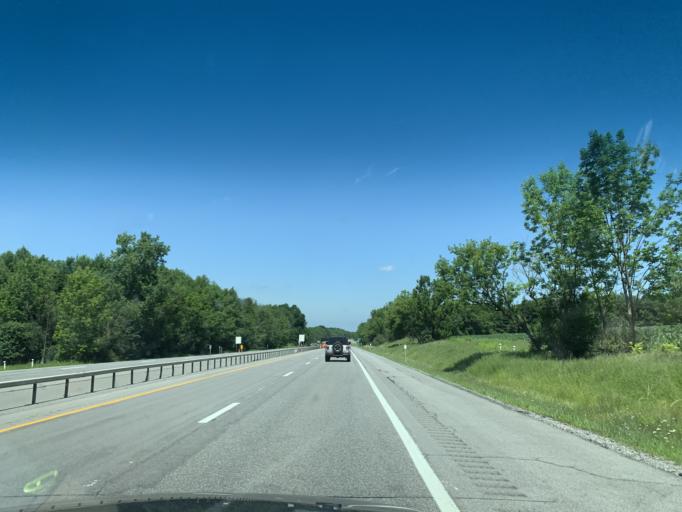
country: US
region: New York
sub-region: Oneida County
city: Chadwicks
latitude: 43.0180
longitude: -75.2569
